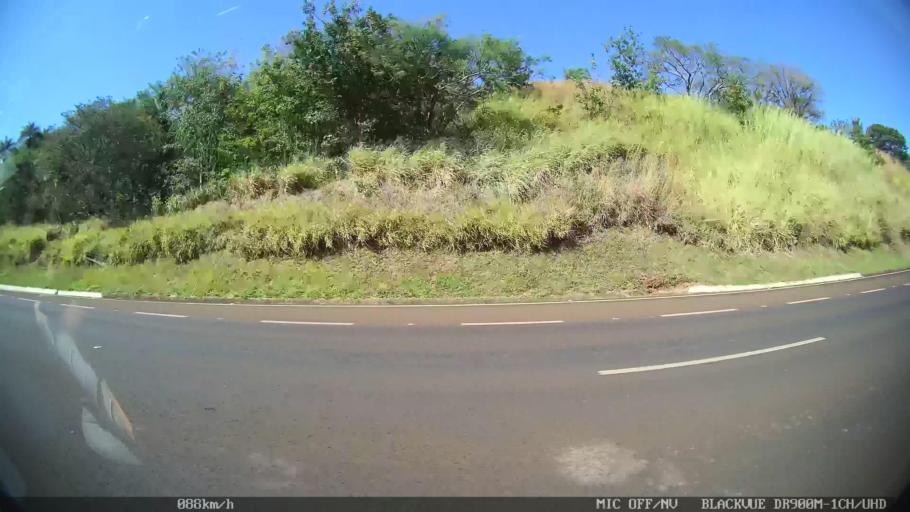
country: BR
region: Sao Paulo
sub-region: Franca
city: Franca
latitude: -20.6070
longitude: -47.4526
